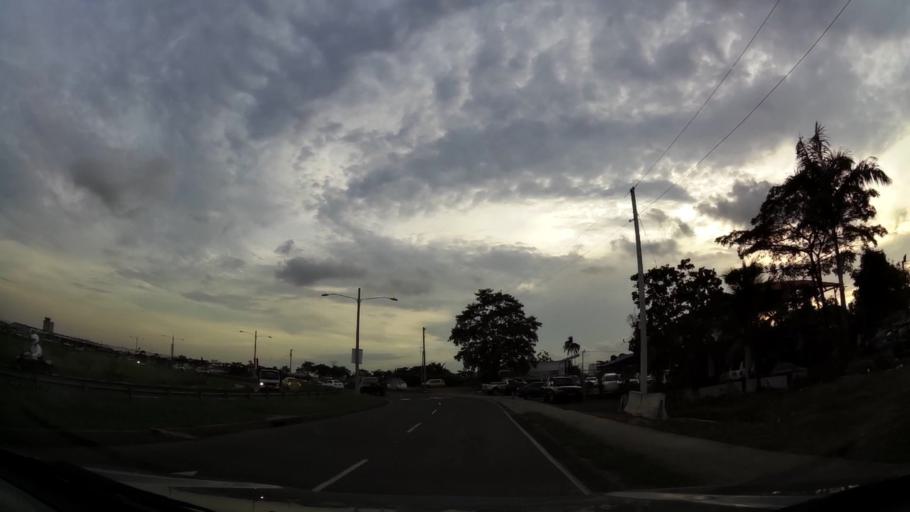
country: PA
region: Panama
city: Tocumen
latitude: 9.0736
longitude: -79.3893
